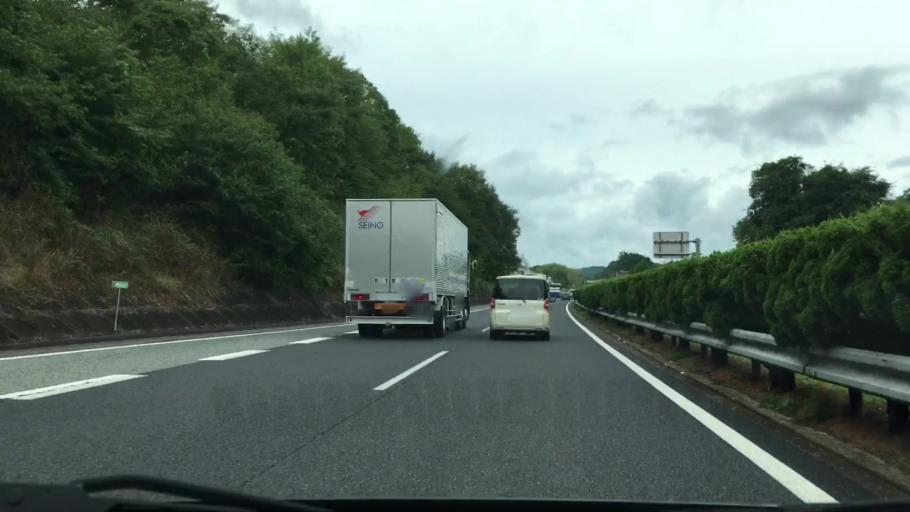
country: JP
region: Okayama
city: Tsuyama
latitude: 35.0277
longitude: 134.1590
